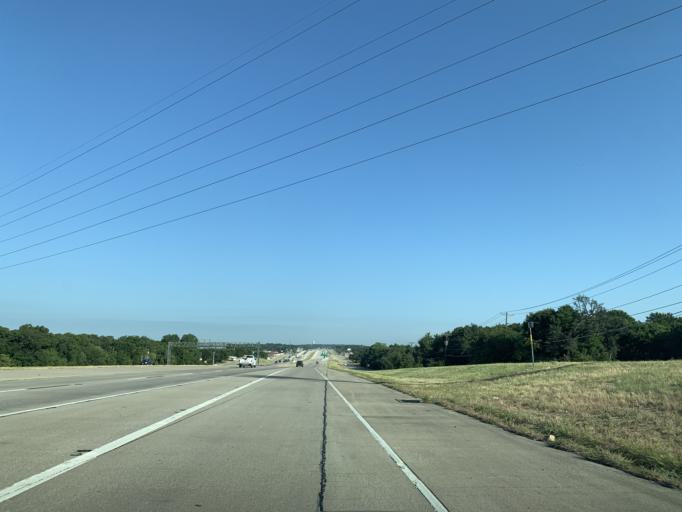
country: US
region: Texas
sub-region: Tarrant County
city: Lakeside
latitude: 32.8302
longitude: -97.4832
